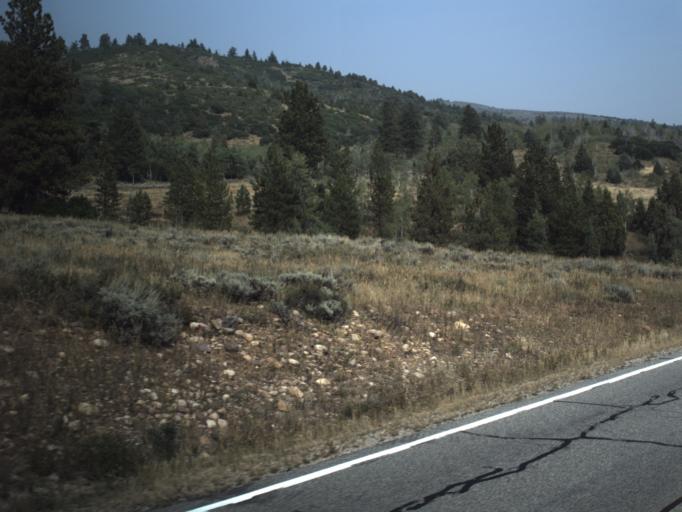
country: US
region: Utah
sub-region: Summit County
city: Kamas
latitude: 40.6289
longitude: -111.1720
